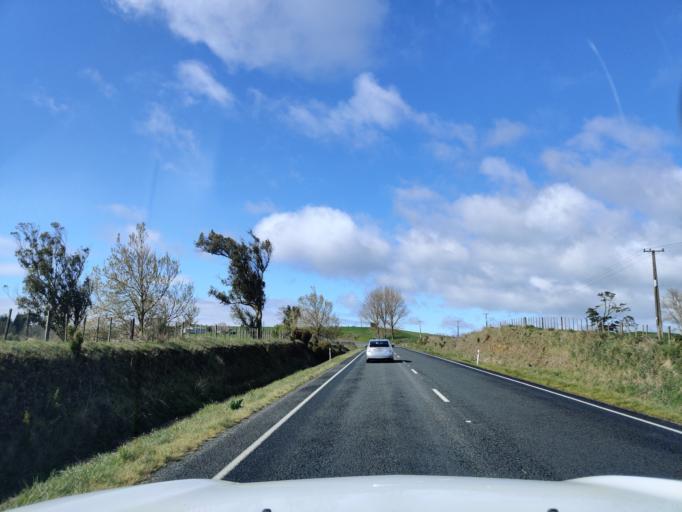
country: NZ
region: Waikato
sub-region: Otorohanga District
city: Otorohanga
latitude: -38.0918
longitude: 175.1824
